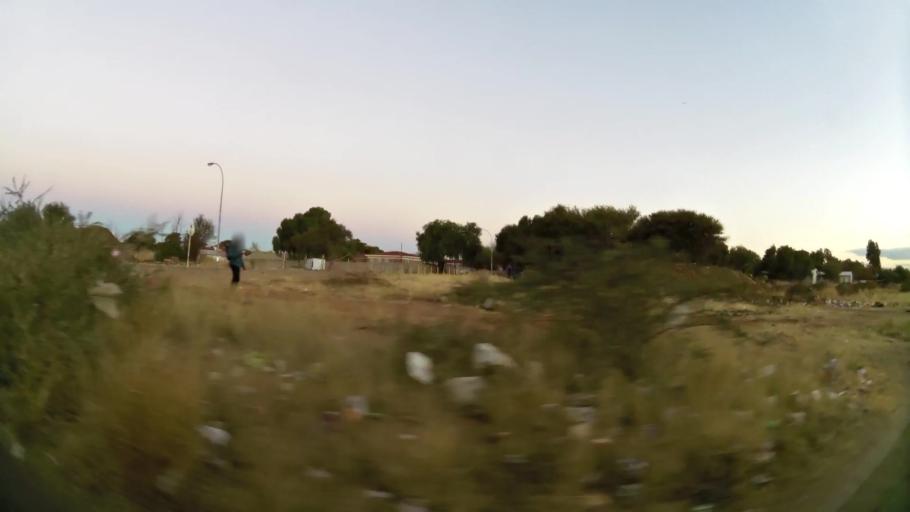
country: ZA
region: Northern Cape
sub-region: Frances Baard District Municipality
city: Kimberley
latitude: -28.7226
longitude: 24.7669
